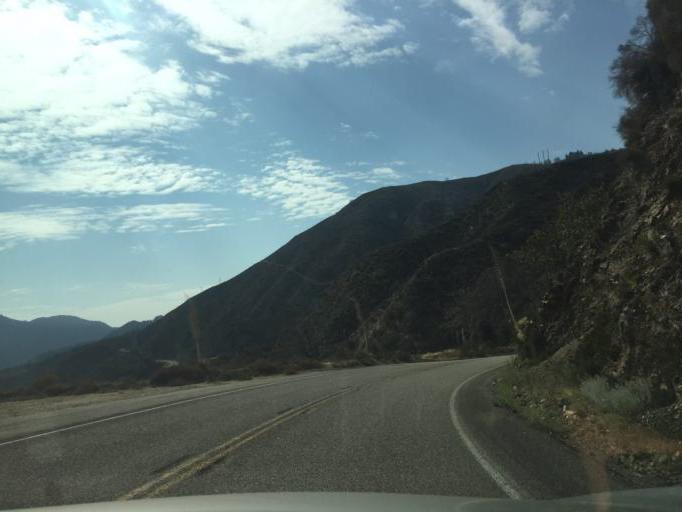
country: US
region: California
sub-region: Los Angeles County
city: Sierra Madre
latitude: 34.2714
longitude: -118.0547
